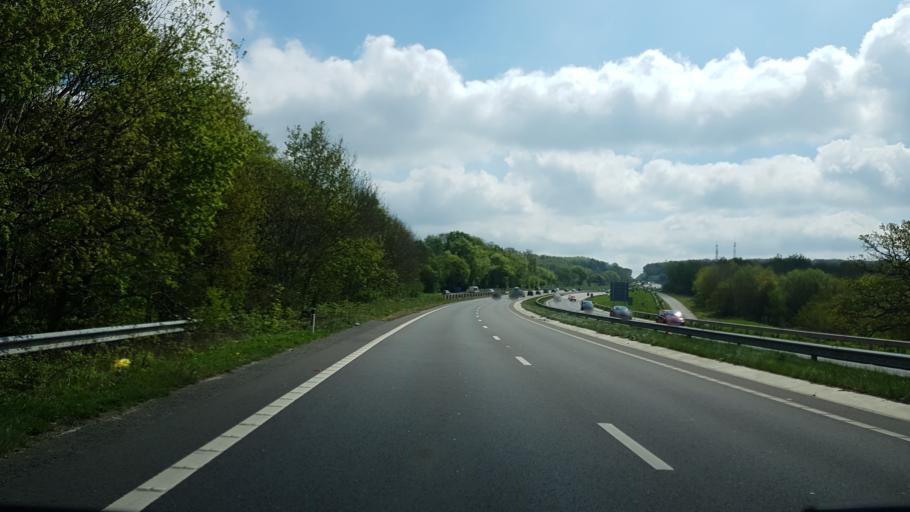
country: GB
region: England
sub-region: Kent
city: Tonbridge
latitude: 51.1804
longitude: 0.2844
